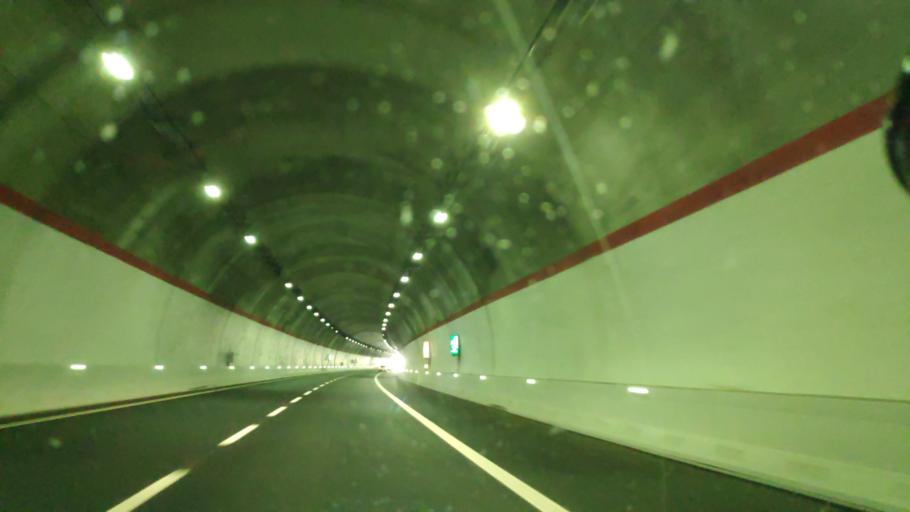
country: IT
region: Campania
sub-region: Provincia di Salerno
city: Casalbuono
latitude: 40.2260
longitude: 15.6710
